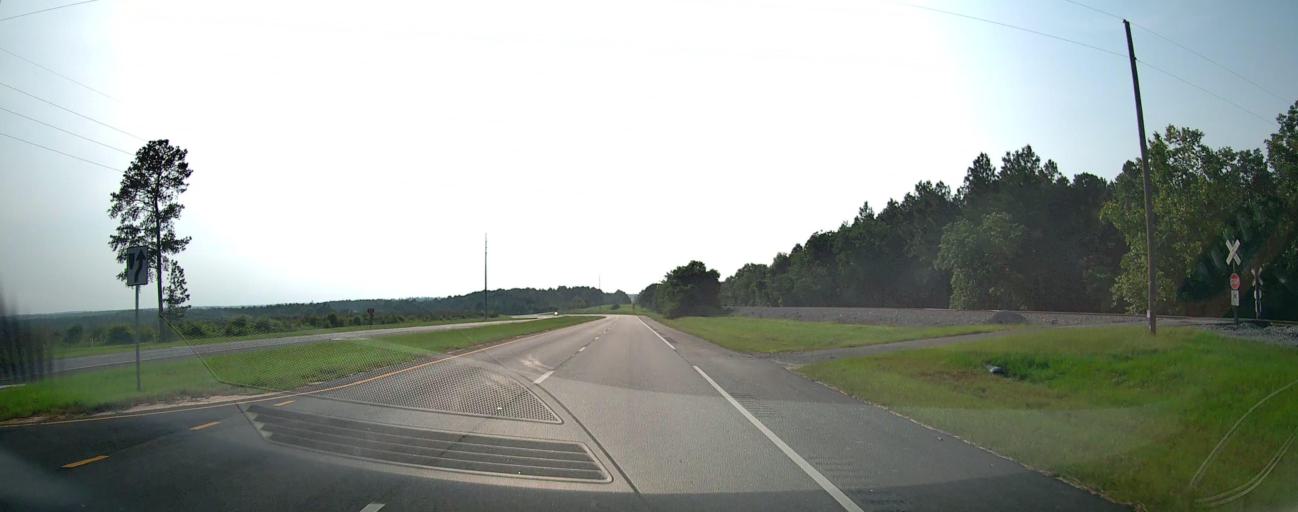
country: US
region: Georgia
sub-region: Taylor County
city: Butler
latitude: 32.5880
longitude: -84.3512
